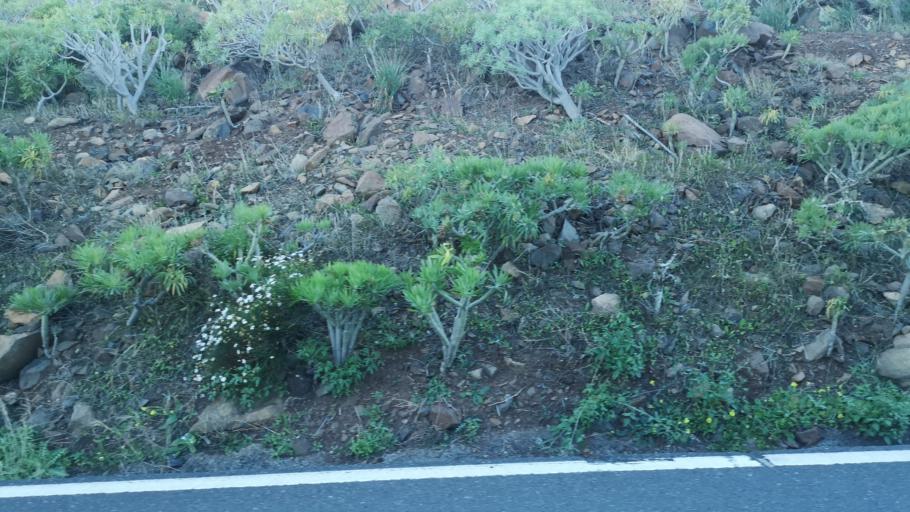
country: ES
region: Canary Islands
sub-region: Provincia de Santa Cruz de Tenerife
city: San Sebastian de la Gomera
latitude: 28.0832
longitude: -17.1308
